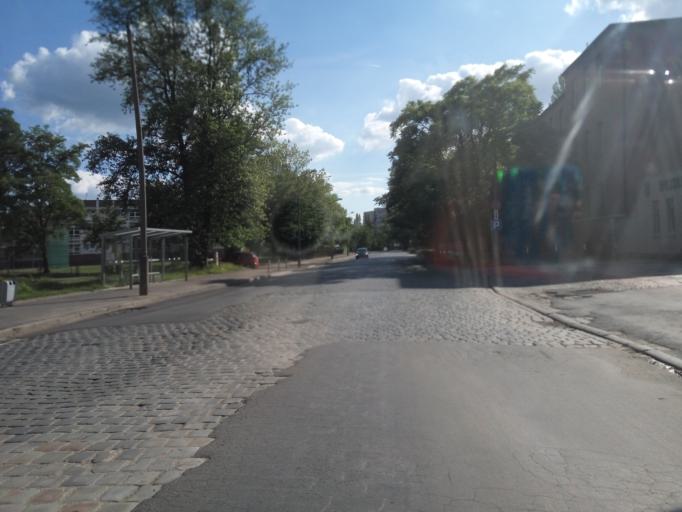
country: PL
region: Lower Silesian Voivodeship
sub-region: Powiat wroclawski
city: Wroclaw
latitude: 51.1202
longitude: 17.0103
